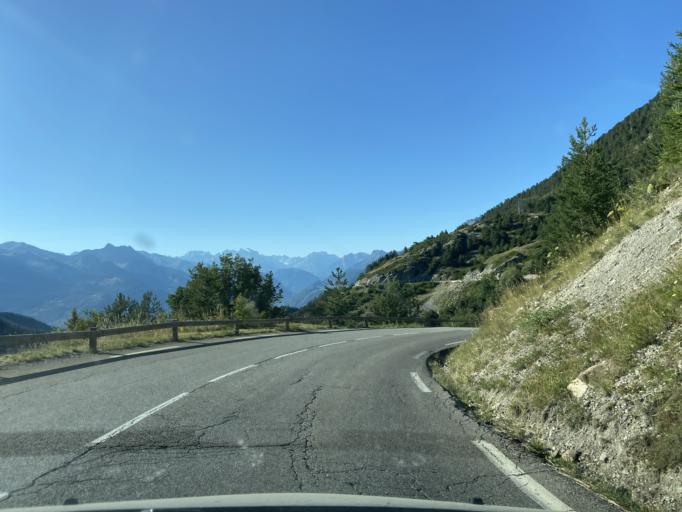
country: FR
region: Provence-Alpes-Cote d'Azur
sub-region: Departement des Hautes-Alpes
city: Guillestre
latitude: 44.6216
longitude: 6.6831
